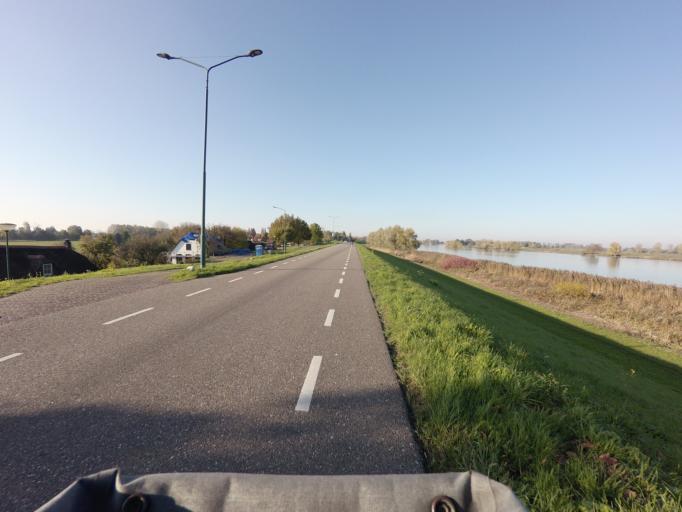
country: NL
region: North Brabant
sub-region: Gemeente Woudrichem
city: Woudrichem
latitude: 51.8048
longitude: 5.0177
